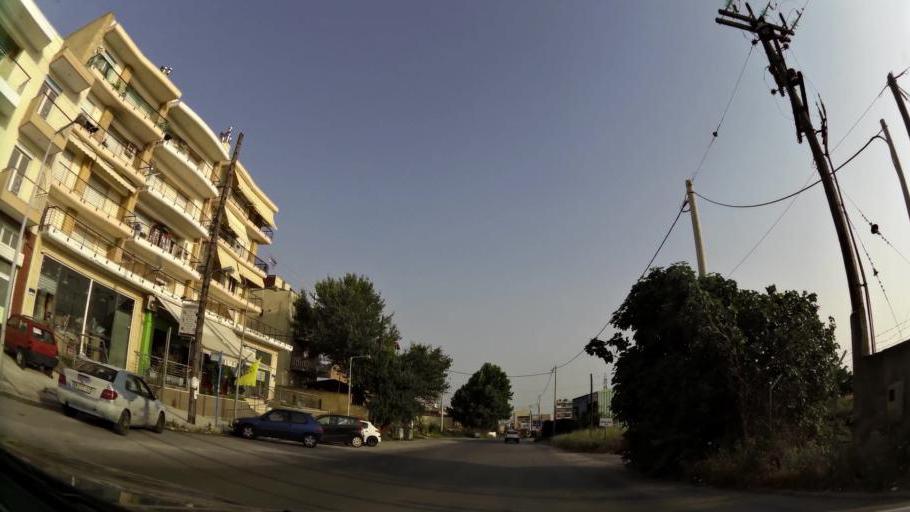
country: GR
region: Central Macedonia
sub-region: Nomos Thessalonikis
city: Evosmos
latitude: 40.6795
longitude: 22.9061
